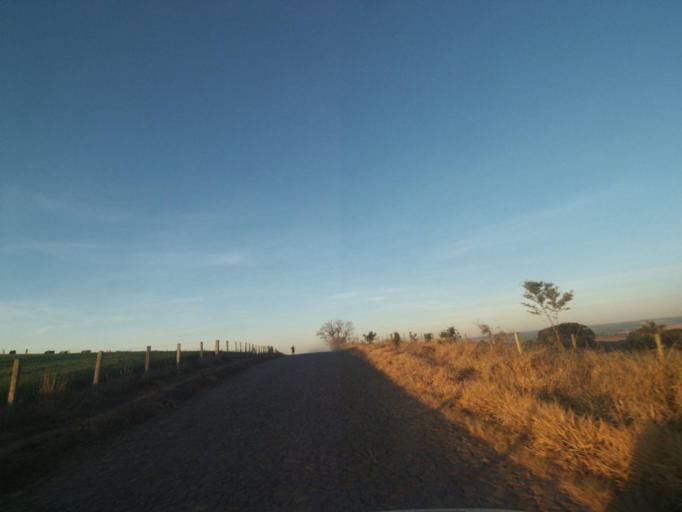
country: BR
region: Parana
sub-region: Tibagi
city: Tibagi
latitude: -24.5276
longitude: -50.4554
